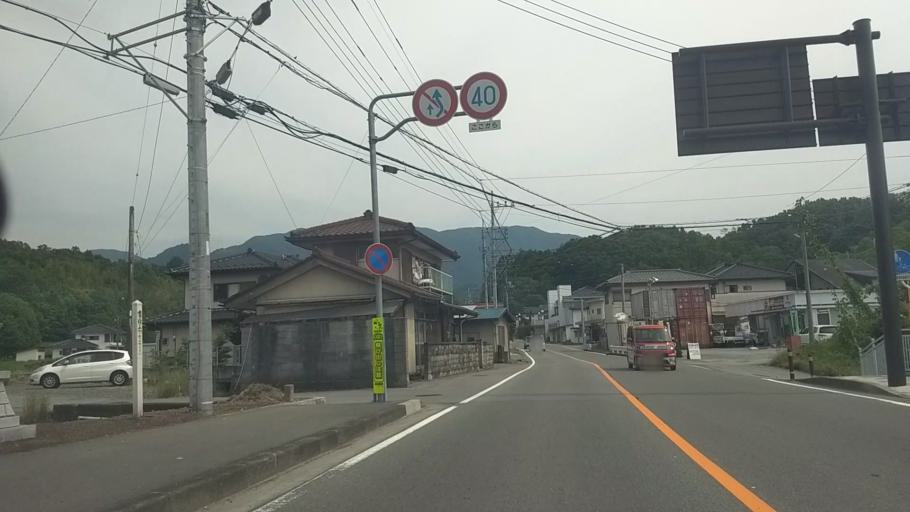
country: JP
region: Yamanashi
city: Isawa
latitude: 35.5951
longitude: 138.5876
